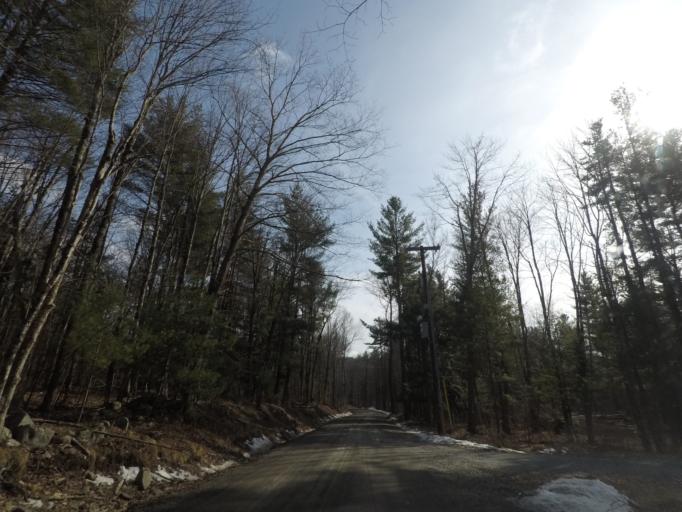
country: US
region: New York
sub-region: Rensselaer County
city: Nassau
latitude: 42.5573
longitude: -73.5543
